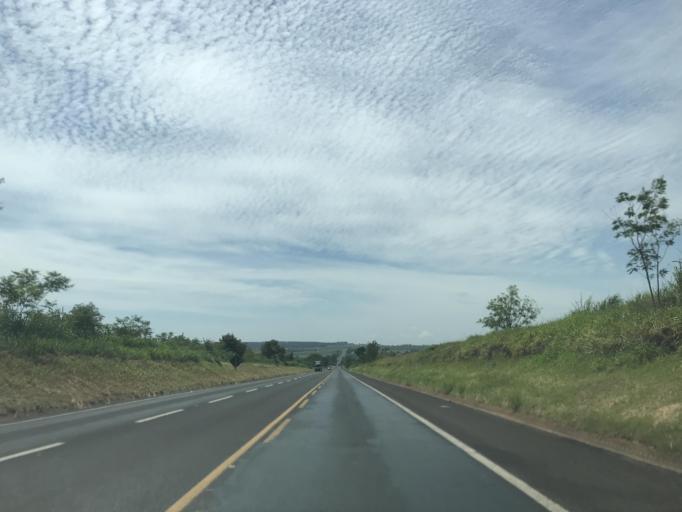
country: BR
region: Parana
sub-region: Paranavai
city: Nova Aurora
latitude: -22.9950
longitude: -52.5863
